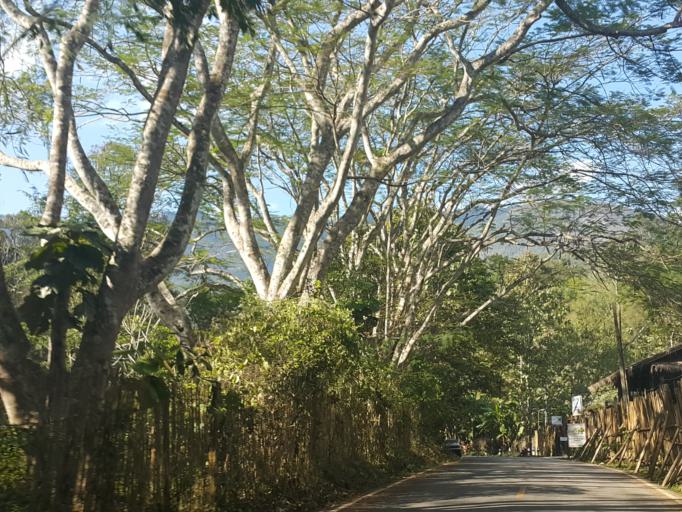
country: TH
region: Chiang Mai
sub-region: Amphoe Chiang Dao
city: Chiang Dao
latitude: 19.4089
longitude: 98.9234
